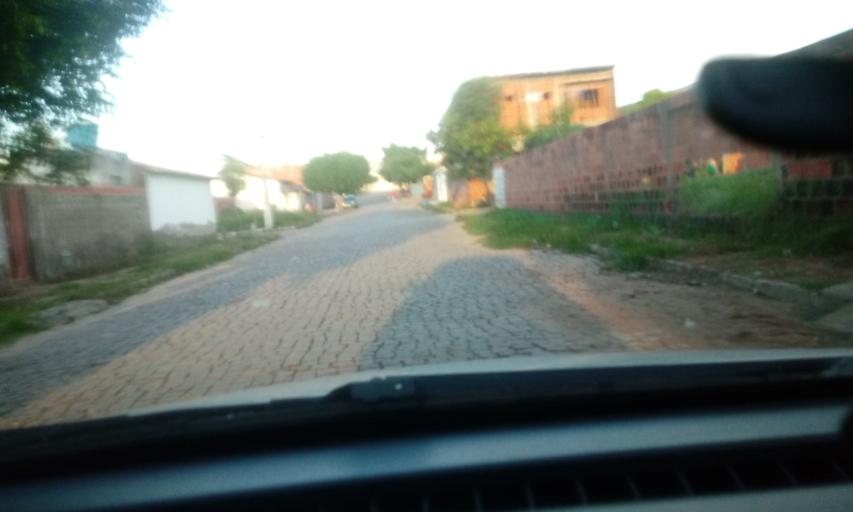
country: BR
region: Bahia
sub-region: Riacho De Santana
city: Riacho de Santana
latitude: -13.9087
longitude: -42.8467
